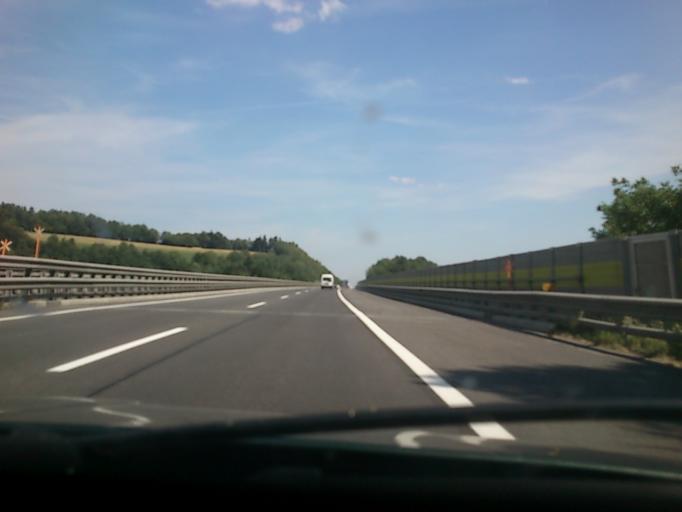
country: AT
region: Lower Austria
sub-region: Politischer Bezirk Neunkirchen
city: Warth
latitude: 47.6499
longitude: 16.1235
